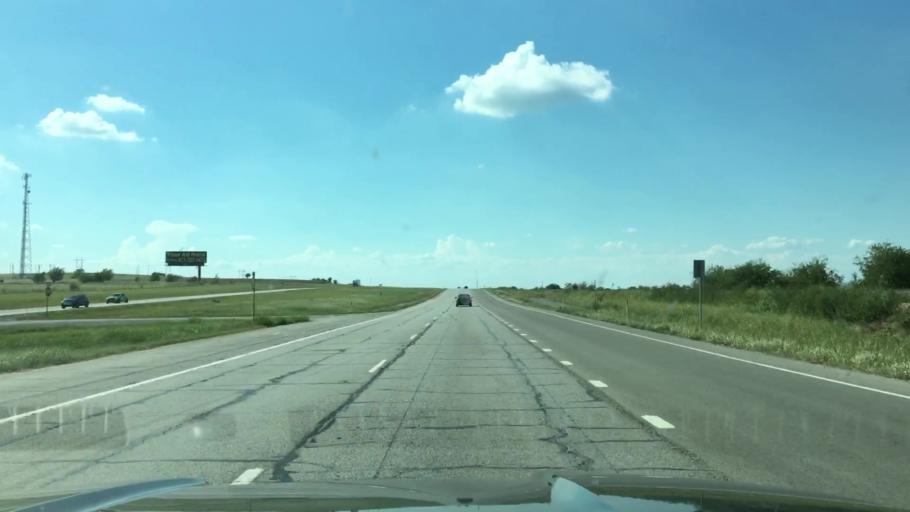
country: US
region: Texas
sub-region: Wise County
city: New Fairview
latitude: 33.1522
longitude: -97.5109
